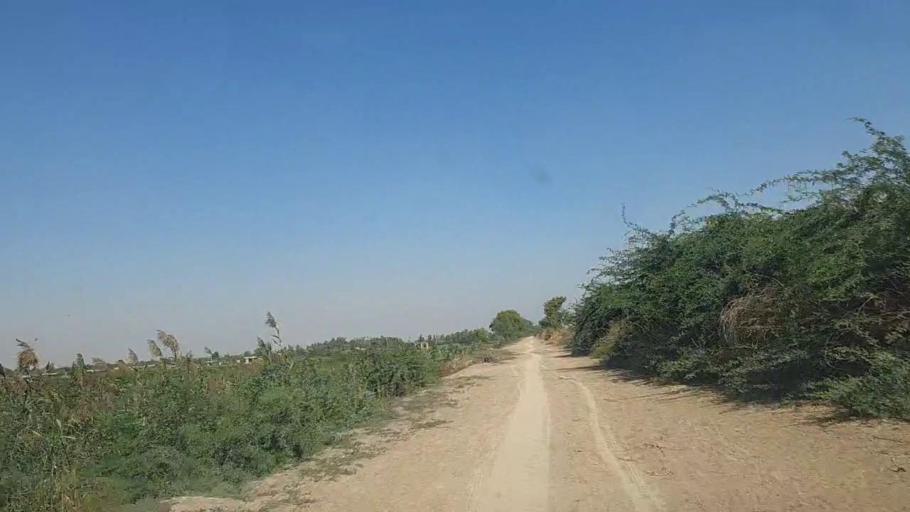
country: PK
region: Sindh
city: Thatta
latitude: 24.7910
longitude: 67.9764
